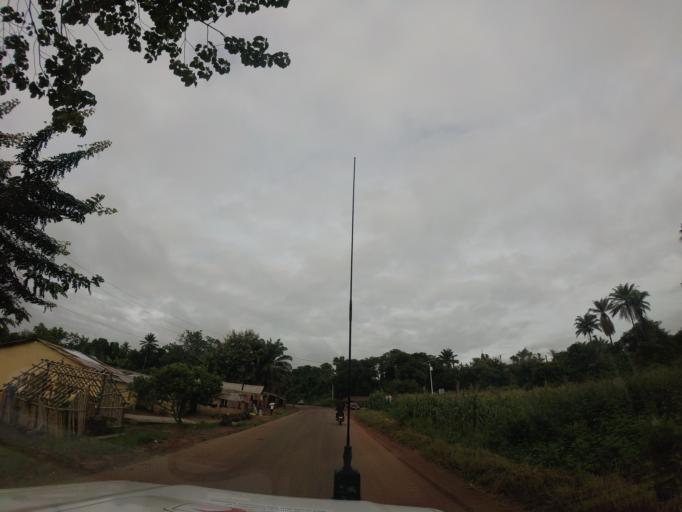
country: GN
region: Kindia
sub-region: Kindia
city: Kindia
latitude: 9.9945
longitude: -12.9084
